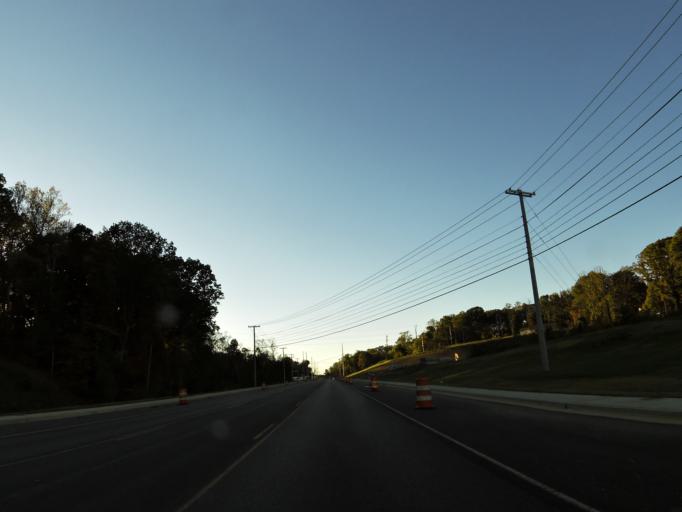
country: US
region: Tennessee
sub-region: Knox County
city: Knoxville
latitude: 35.9814
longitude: -84.0194
